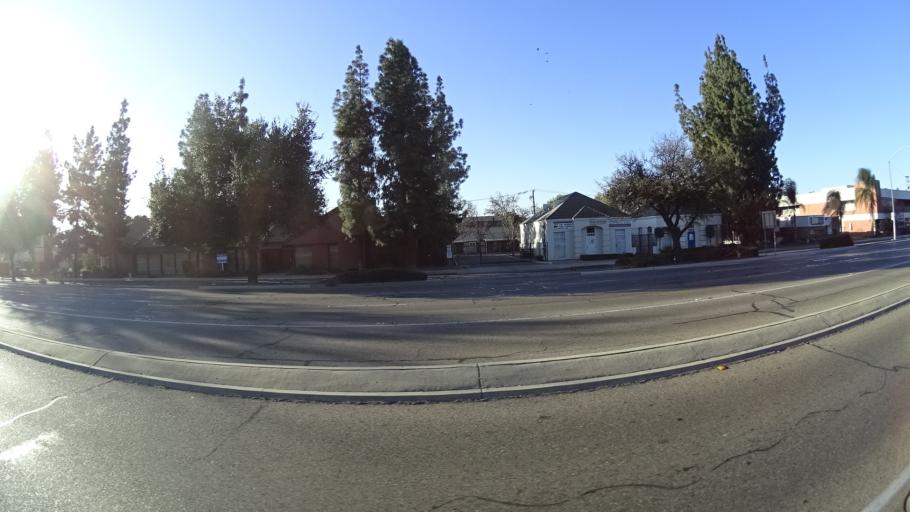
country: US
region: California
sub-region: Fresno County
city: Fresno
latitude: 36.8087
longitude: -119.7689
